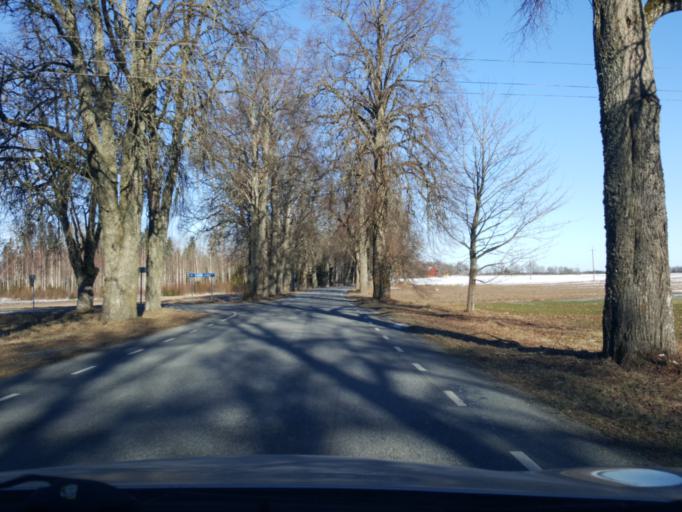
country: EE
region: Viljandimaa
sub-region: Vohma linn
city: Vohma
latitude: 58.5343
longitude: 25.5828
